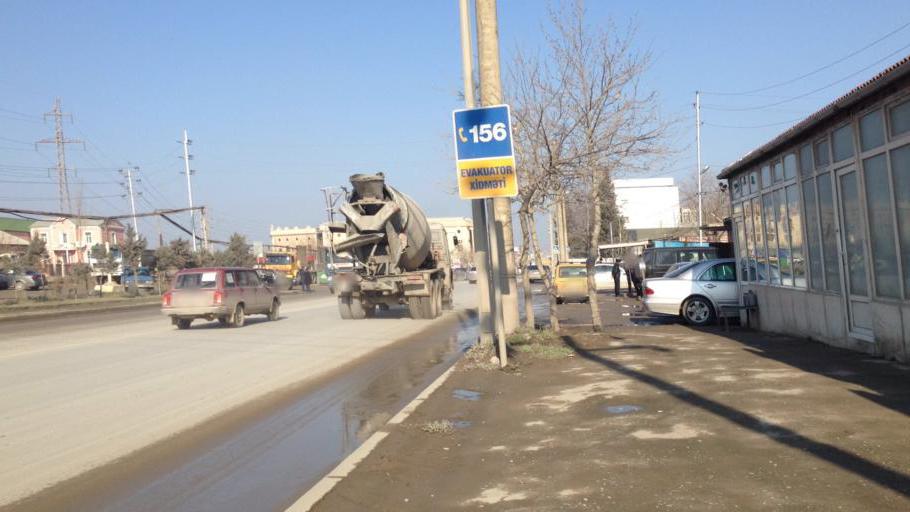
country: AZ
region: Baki
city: Binagadi
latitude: 40.4427
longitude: 49.8447
